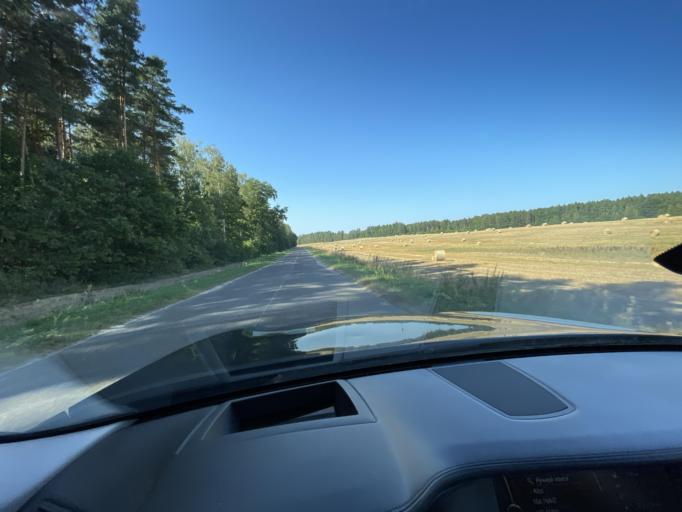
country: BY
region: Grodnenskaya
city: Hrodna
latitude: 53.7539
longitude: 23.9717
